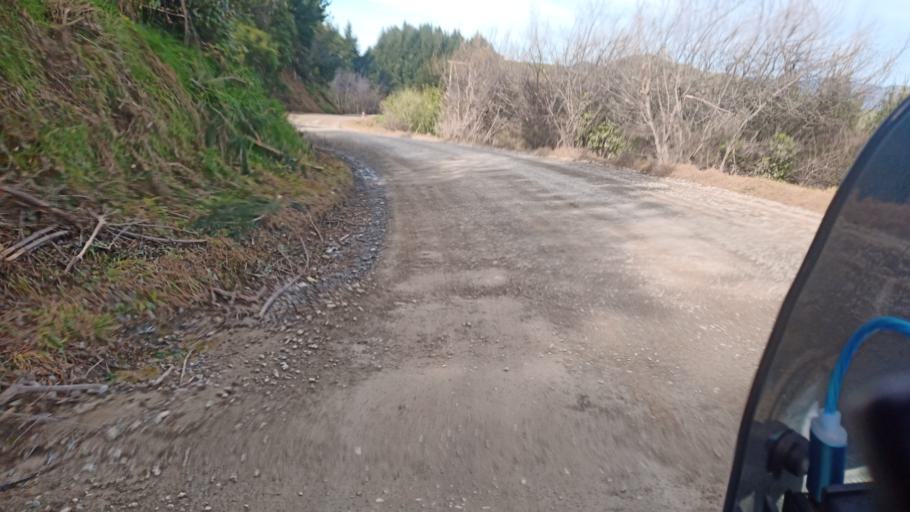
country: NZ
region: Gisborne
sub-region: Gisborne District
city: Gisborne
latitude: -38.1399
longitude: 178.1954
